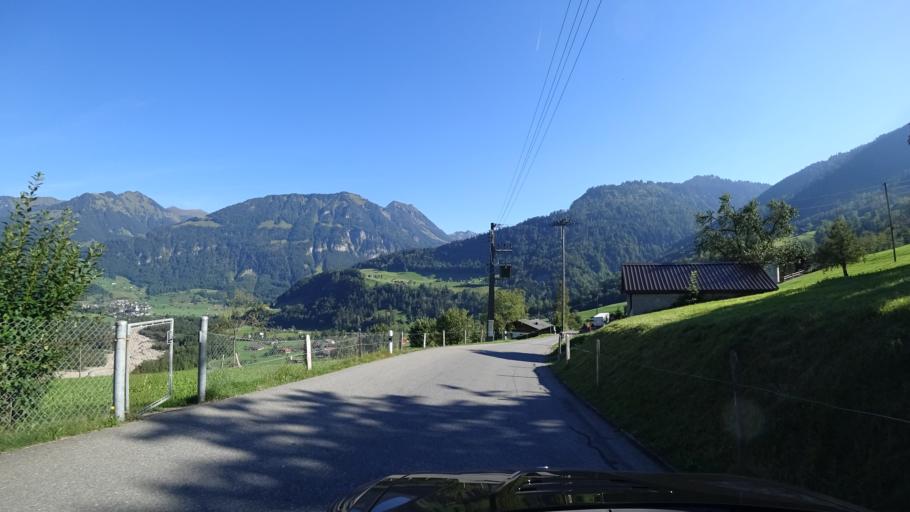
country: CH
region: Obwalden
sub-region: Obwalden
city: Giswil
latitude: 46.8365
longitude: 8.1481
